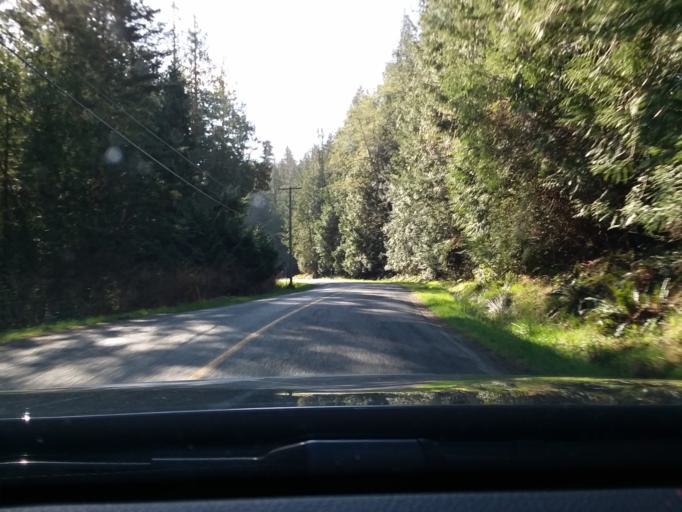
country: CA
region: British Columbia
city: North Cowichan
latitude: 48.9265
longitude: -123.4546
